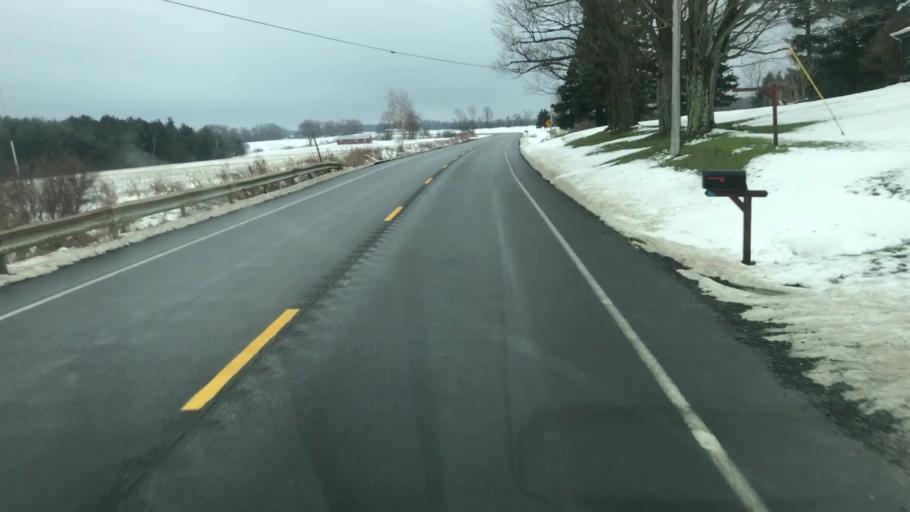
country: US
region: New York
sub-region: Cayuga County
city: Moravia
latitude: 42.7921
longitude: -76.3467
